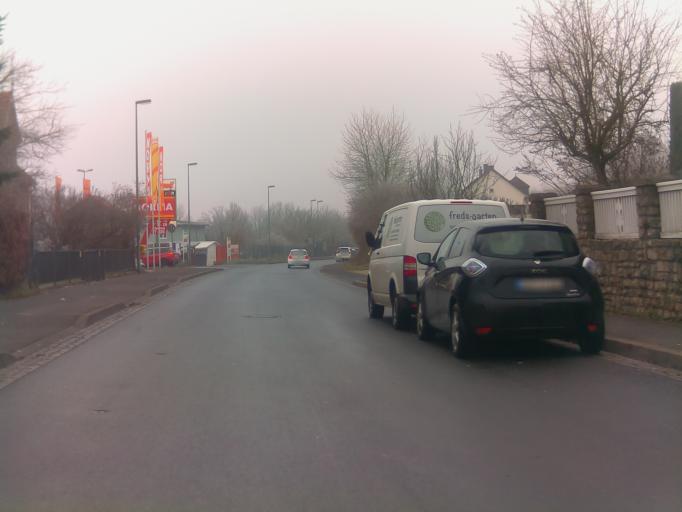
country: DE
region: Bavaria
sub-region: Regierungsbezirk Unterfranken
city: Kitzingen
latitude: 49.7267
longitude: 10.1557
